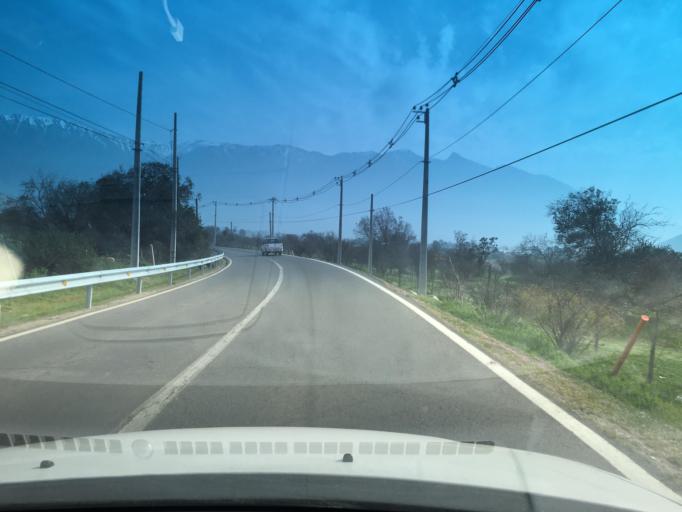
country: CL
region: Santiago Metropolitan
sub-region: Provincia de Chacabuco
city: Lampa
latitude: -33.2510
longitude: -70.9081
